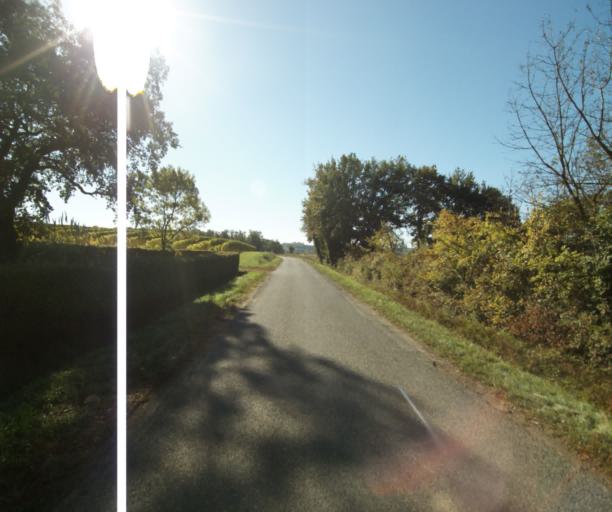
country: FR
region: Midi-Pyrenees
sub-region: Departement du Gers
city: Gondrin
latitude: 43.8193
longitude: 0.2190
